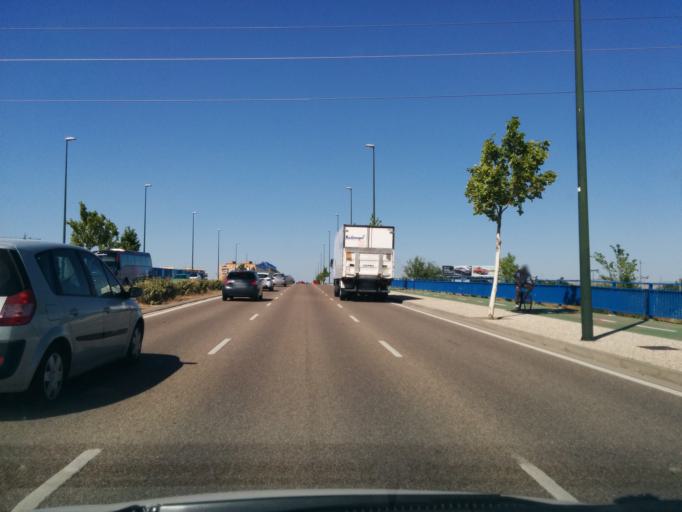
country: ES
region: Aragon
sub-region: Provincia de Zaragoza
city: Zaragoza
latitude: 41.6310
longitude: -0.8670
